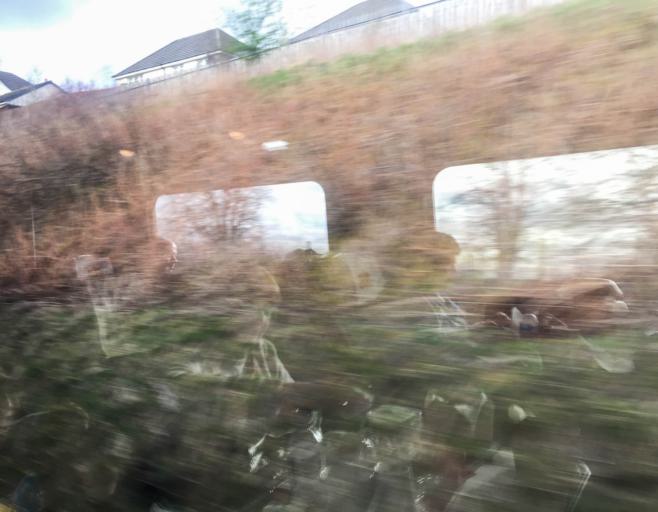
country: GB
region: Scotland
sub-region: South Lanarkshire
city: Carluke
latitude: 55.7374
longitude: -3.8580
